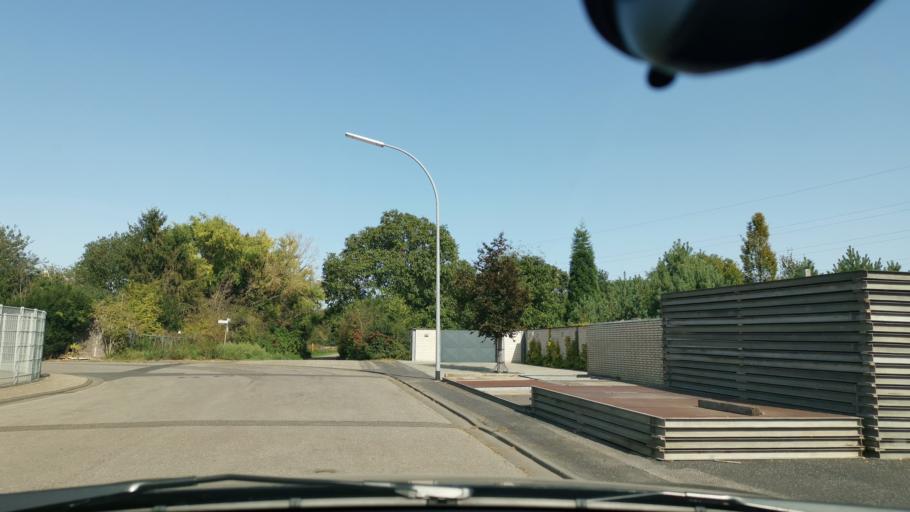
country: DE
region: North Rhine-Westphalia
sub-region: Regierungsbezirk Dusseldorf
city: Grevenbroich
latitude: 51.1049
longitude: 6.5920
